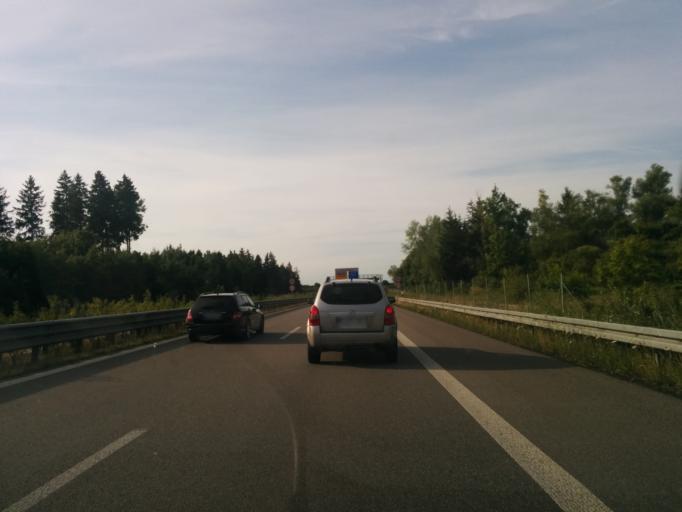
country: DE
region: Bavaria
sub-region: Upper Bavaria
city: Landsberg am Lech
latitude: 48.0549
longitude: 10.8335
